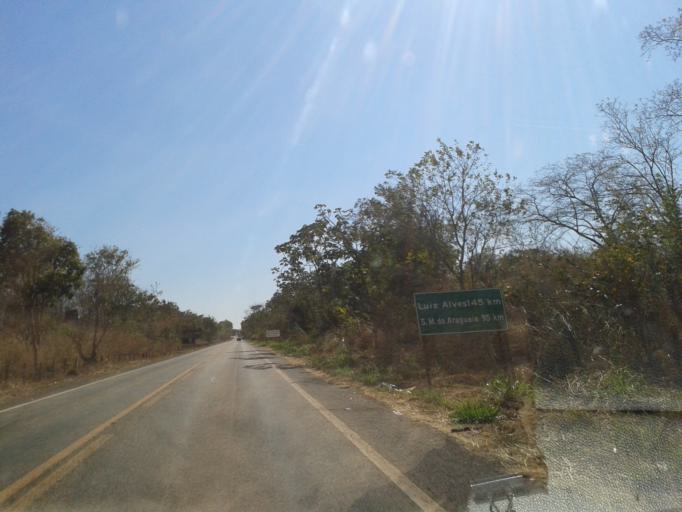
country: BR
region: Goias
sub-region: Crixas
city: Crixas
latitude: -14.0863
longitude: -50.3348
